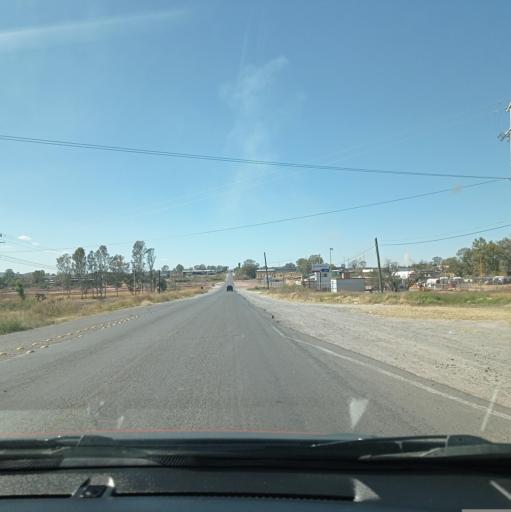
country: MX
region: Jalisco
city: San Julian
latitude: 21.0075
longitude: -102.1473
